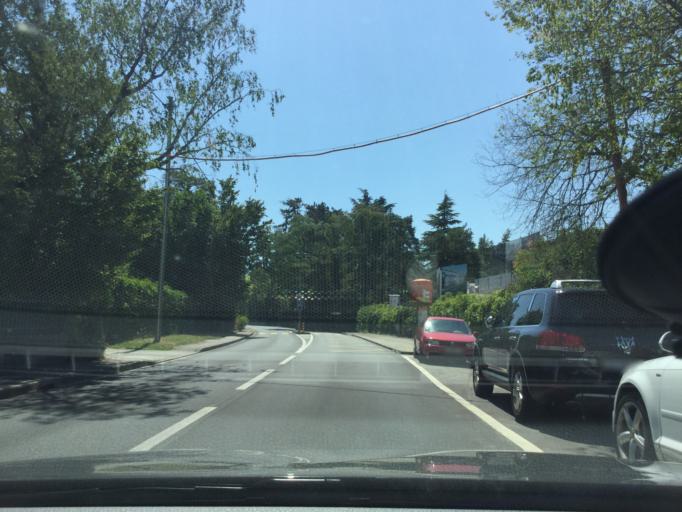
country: CH
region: Geneva
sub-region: Geneva
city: Vandoeuvres
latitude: 46.2437
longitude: 6.1987
